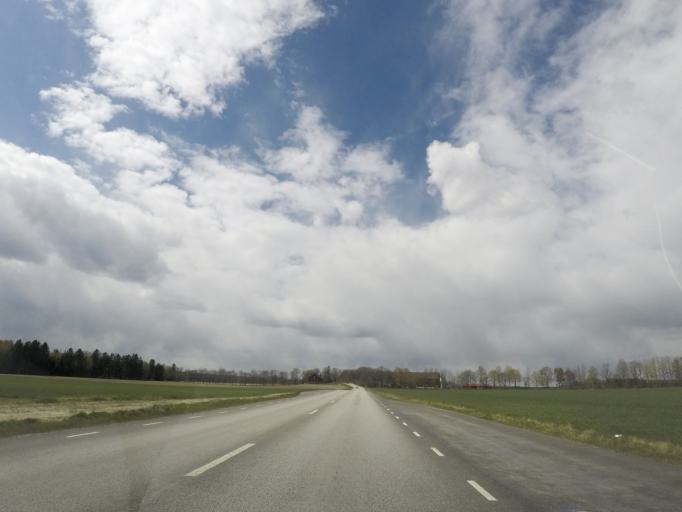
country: SE
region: Soedermanland
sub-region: Nykopings Kommun
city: Svalsta
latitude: 58.7413
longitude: 16.8144
